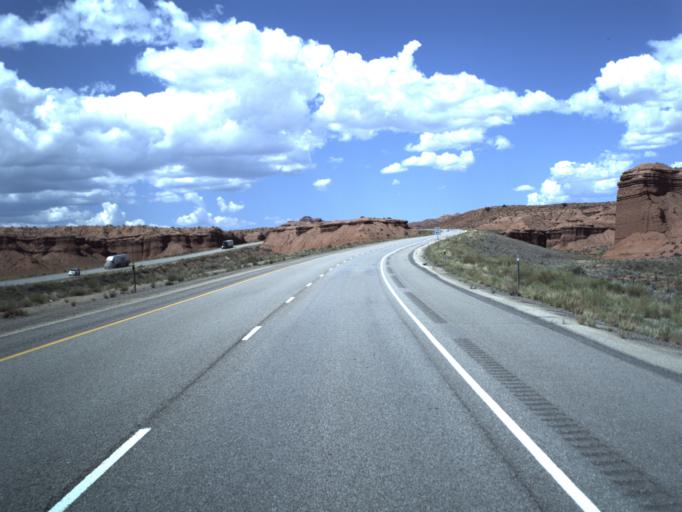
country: US
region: Utah
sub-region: Emery County
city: Ferron
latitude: 38.8391
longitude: -111.0770
